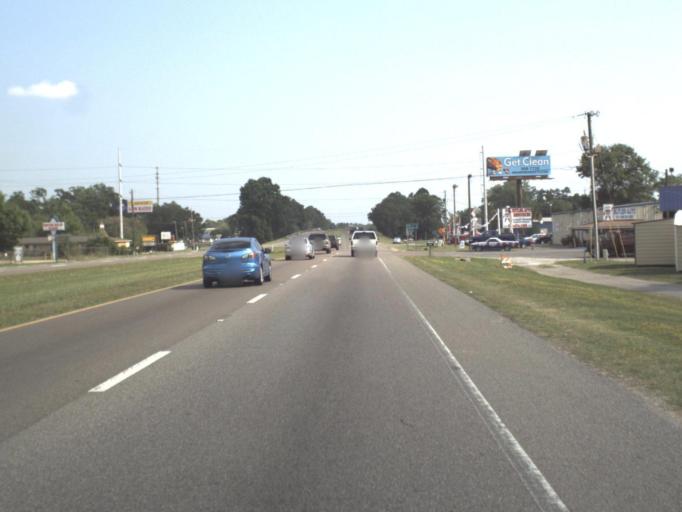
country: US
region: Florida
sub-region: Escambia County
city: Ensley
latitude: 30.5376
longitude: -87.2794
